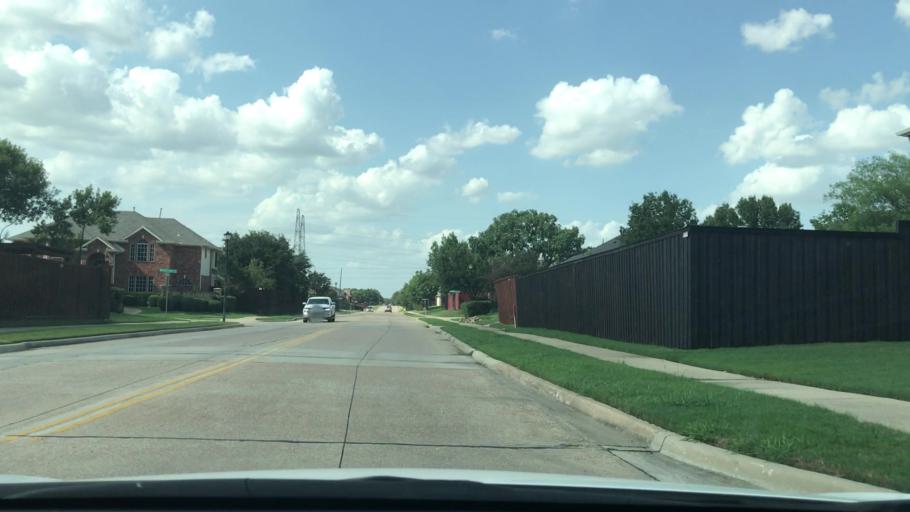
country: US
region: Texas
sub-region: Dallas County
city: Carrollton
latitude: 32.9742
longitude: -96.8643
